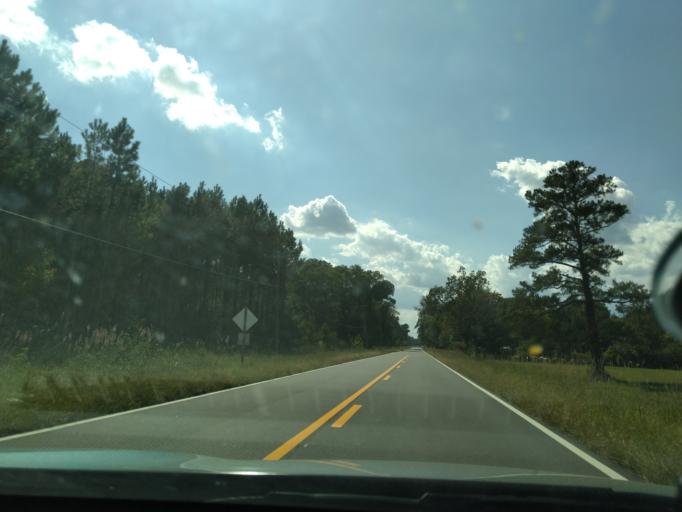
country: US
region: North Carolina
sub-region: Pitt County
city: Bethel
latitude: 35.8100
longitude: -77.3569
